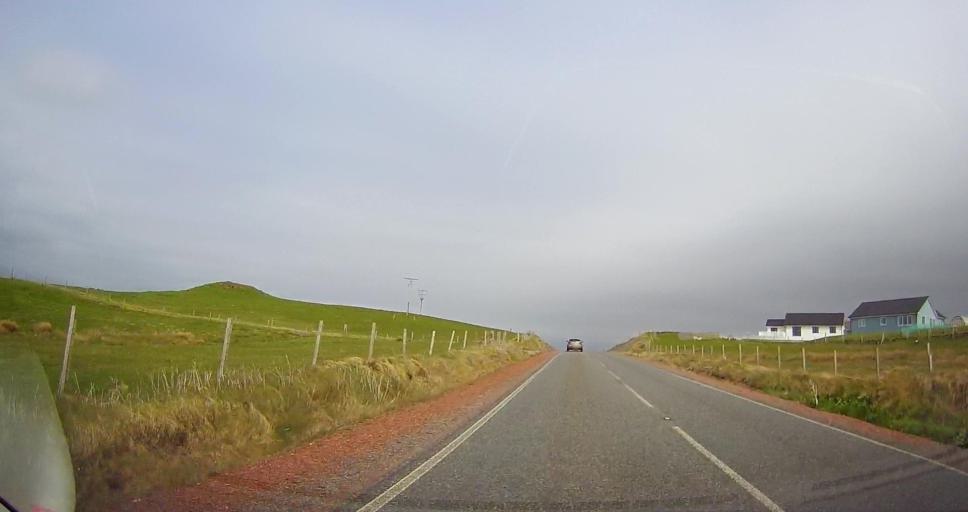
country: GB
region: Scotland
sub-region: Shetland Islands
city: Sandwick
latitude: 60.1196
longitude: -1.2897
